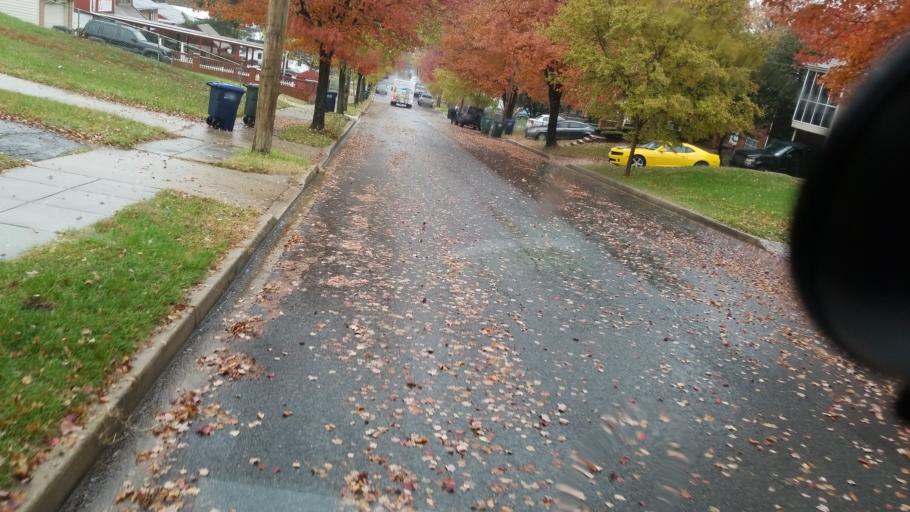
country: US
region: Maryland
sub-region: Prince George's County
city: Capitol Heights
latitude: 38.8866
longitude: -76.9386
